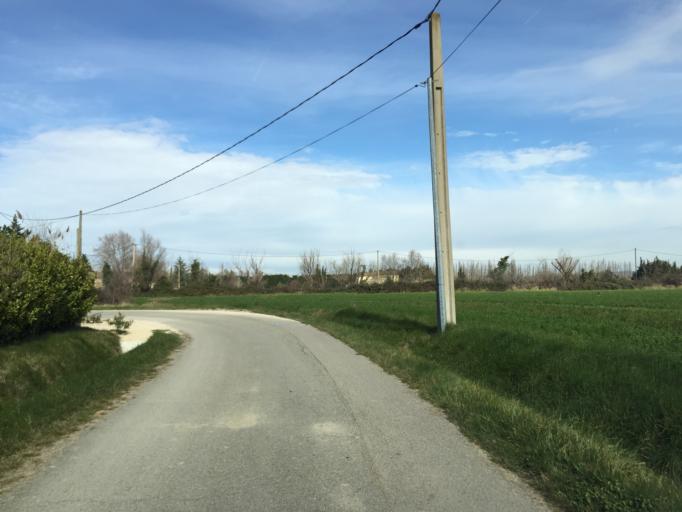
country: FR
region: Provence-Alpes-Cote d'Azur
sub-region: Departement du Vaucluse
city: Caderousse
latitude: 44.1246
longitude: 4.7419
